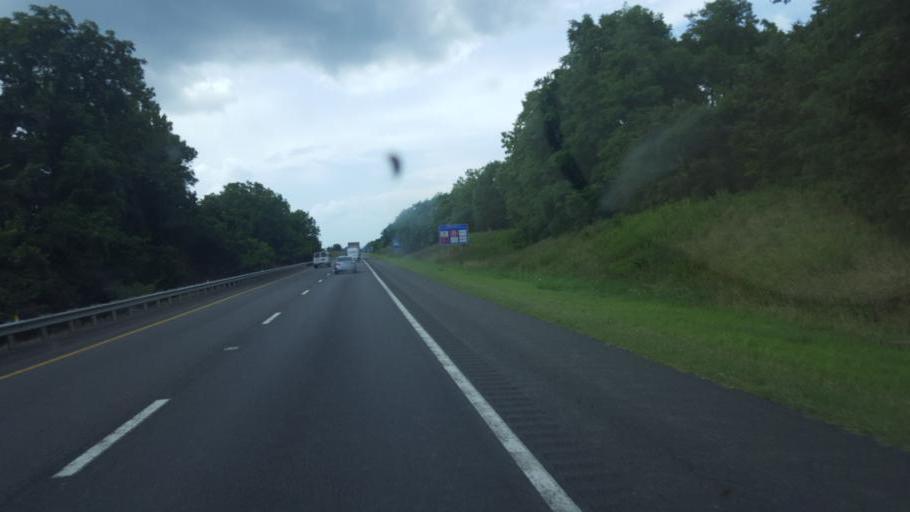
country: US
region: Virginia
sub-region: Warren County
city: Front Royal
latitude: 38.9492
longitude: -78.1622
